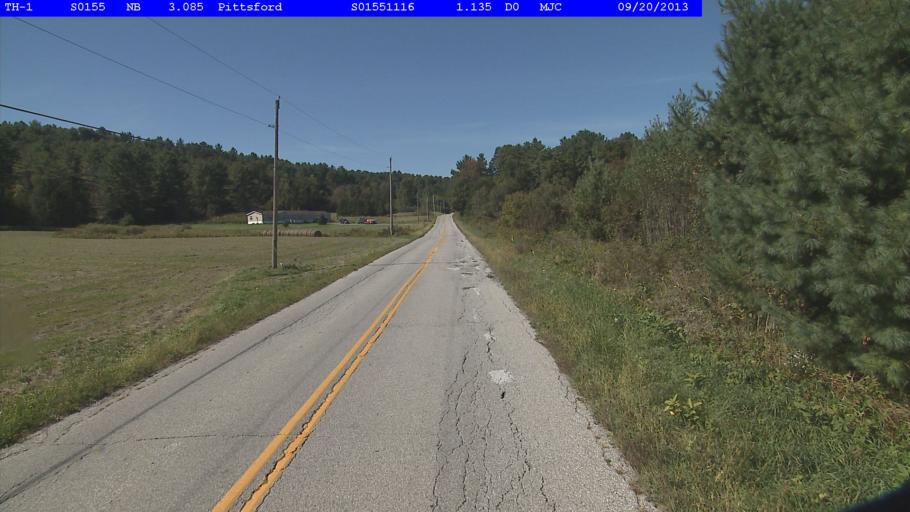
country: US
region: Vermont
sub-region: Rutland County
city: Brandon
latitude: 43.7065
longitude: -73.0509
